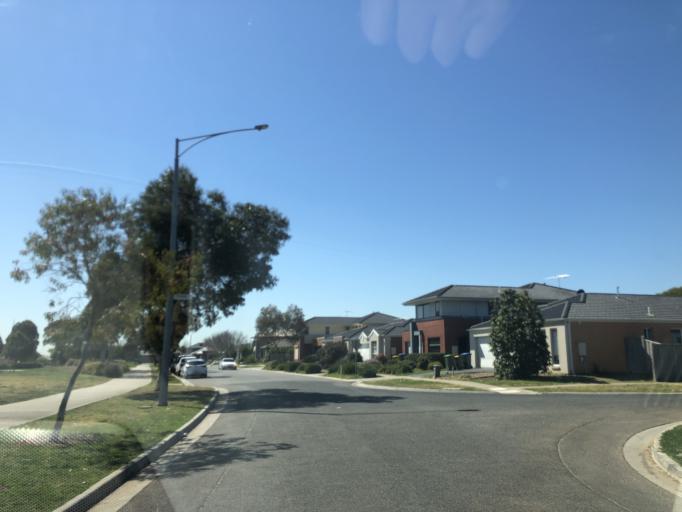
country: AU
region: Victoria
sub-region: Wyndham
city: Point Cook
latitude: -37.9003
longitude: 144.7312
